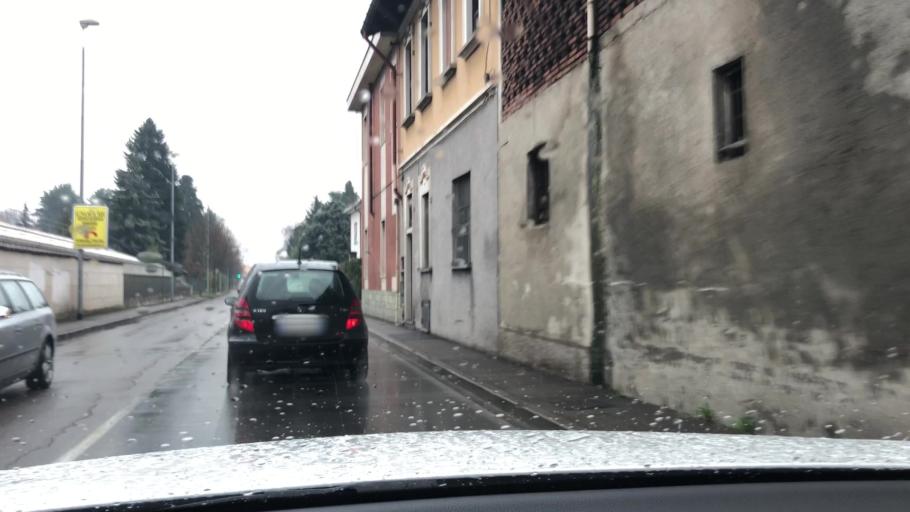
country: IT
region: Lombardy
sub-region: Provincia di Monza e Brianza
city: Nova Milanese
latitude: 45.5894
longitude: 9.2032
